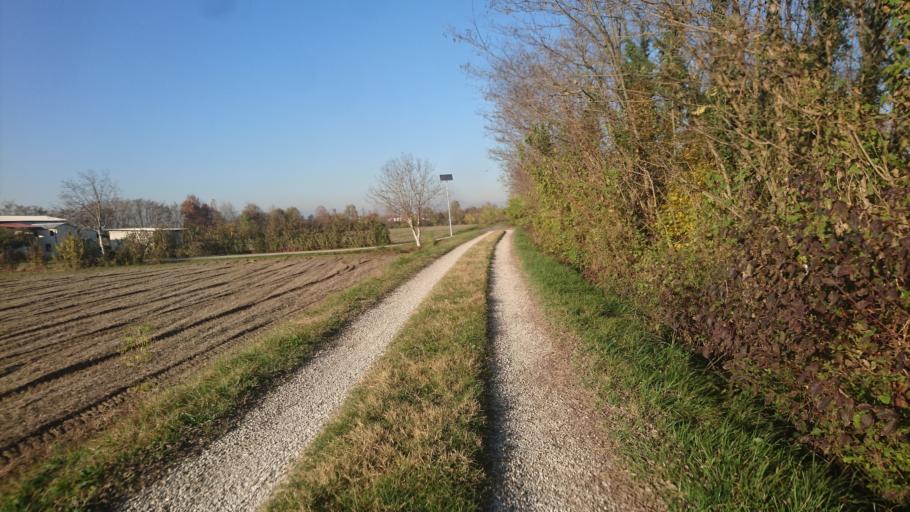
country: IT
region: Veneto
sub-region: Provincia di Padova
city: Villaguattera
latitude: 45.4398
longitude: 11.8284
